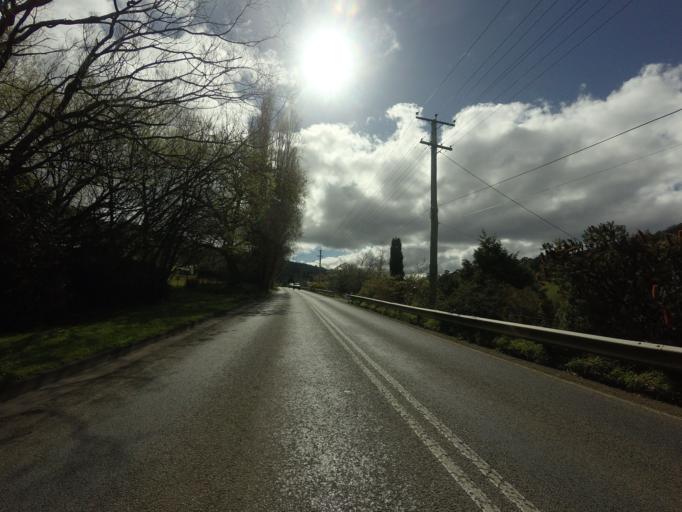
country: AU
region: Tasmania
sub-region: Huon Valley
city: Cygnet
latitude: -43.3094
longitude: 147.0127
